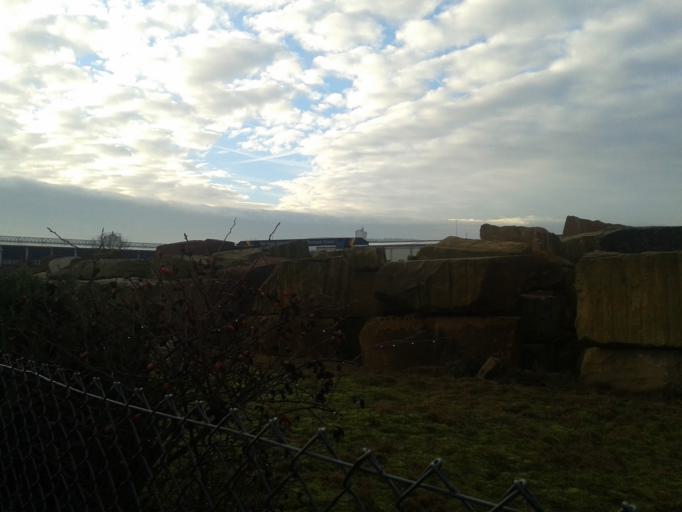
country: DE
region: Bavaria
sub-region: Upper Franconia
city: Hallstadt
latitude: 49.9148
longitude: 10.8738
